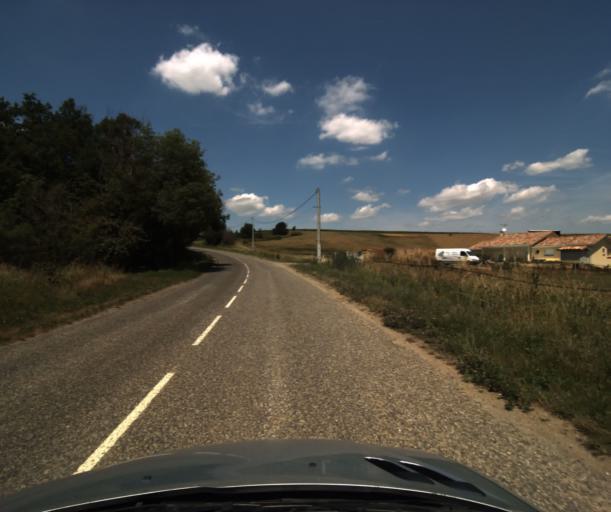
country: FR
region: Midi-Pyrenees
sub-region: Departement de la Haute-Garonne
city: Saint-Lys
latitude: 43.4914
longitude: 1.2105
